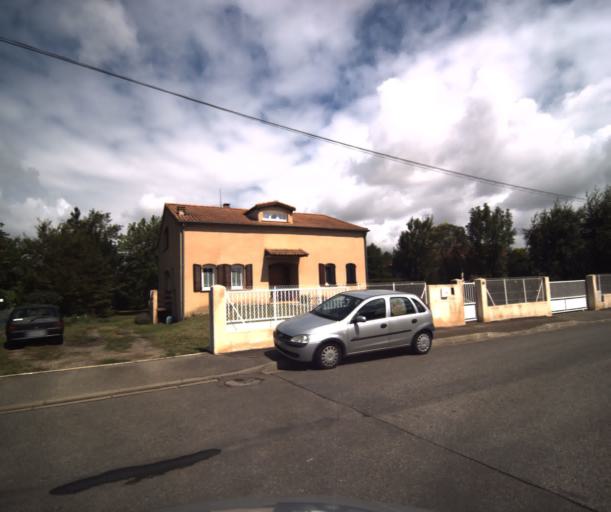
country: FR
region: Midi-Pyrenees
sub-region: Departement de la Haute-Garonne
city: Portet-sur-Garonne
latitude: 43.5178
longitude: 1.3971
